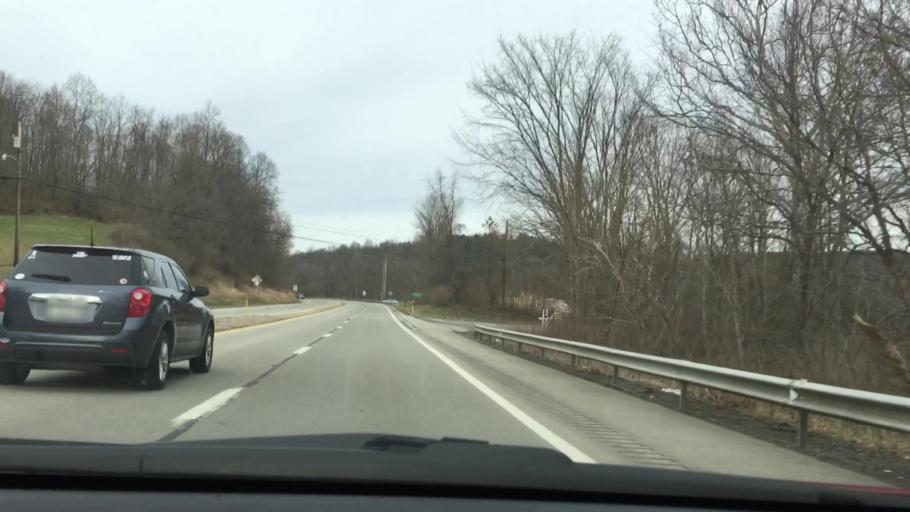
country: US
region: Pennsylvania
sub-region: Fayette County
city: Perryopolis
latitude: 40.0025
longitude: -79.7614
